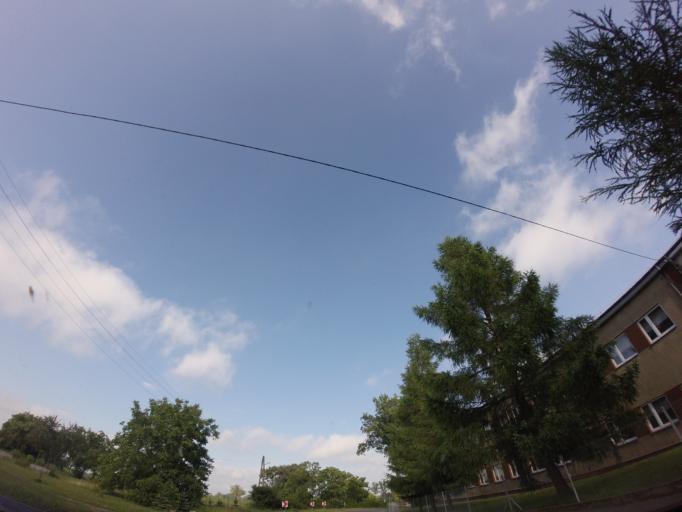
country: PL
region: Lodz Voivodeship
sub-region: Powiat kutnowski
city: Lanieta
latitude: 52.3630
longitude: 19.2781
